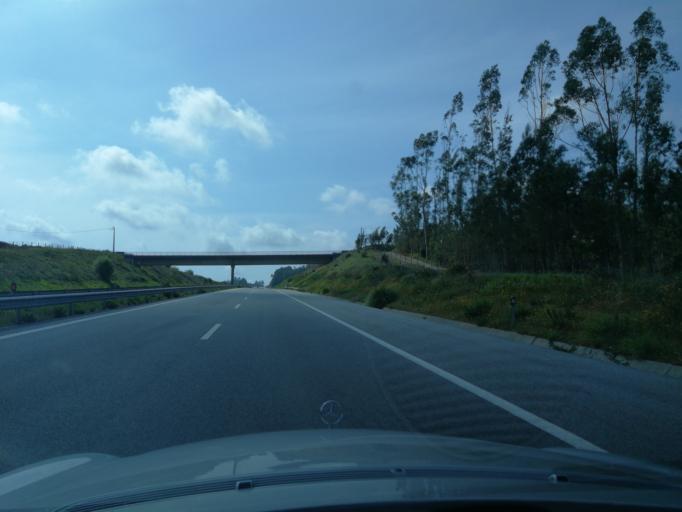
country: PT
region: Braga
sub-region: Vila Nova de Famalicao
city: Ribeirao
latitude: 41.3821
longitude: -8.6384
